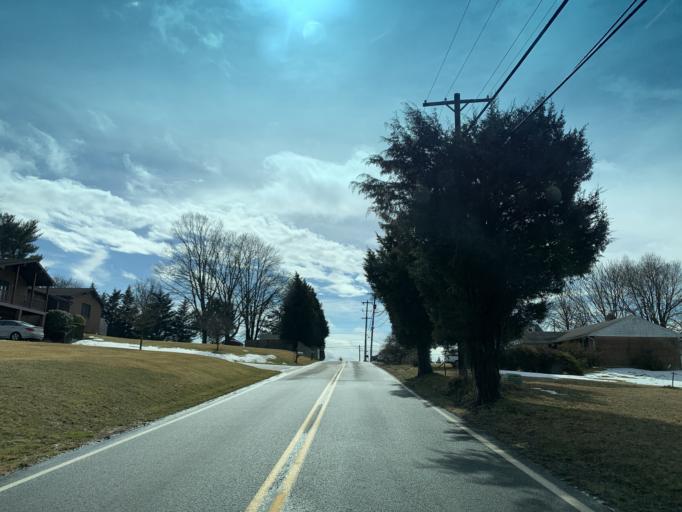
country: US
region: Delaware
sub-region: New Castle County
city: Newark
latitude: 39.6983
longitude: -75.8005
